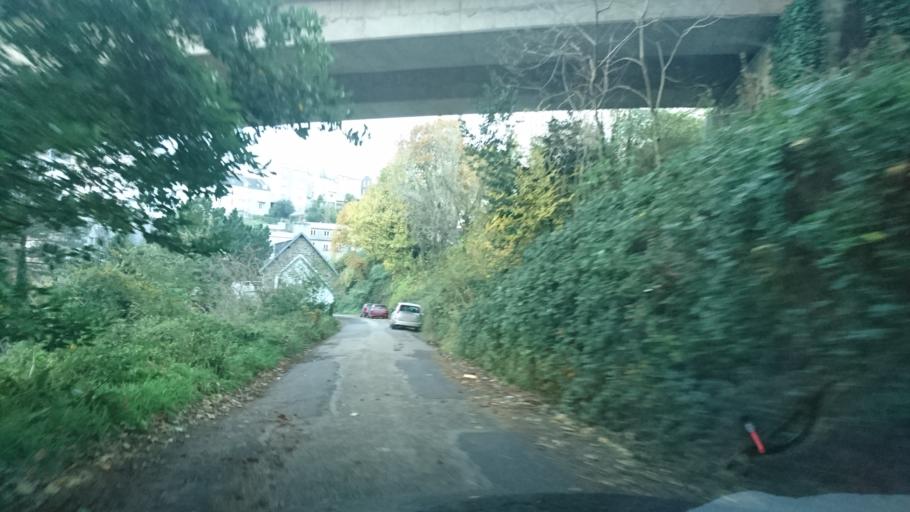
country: FR
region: Brittany
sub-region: Departement du Finistere
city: Brest
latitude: 48.3900
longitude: -4.4691
